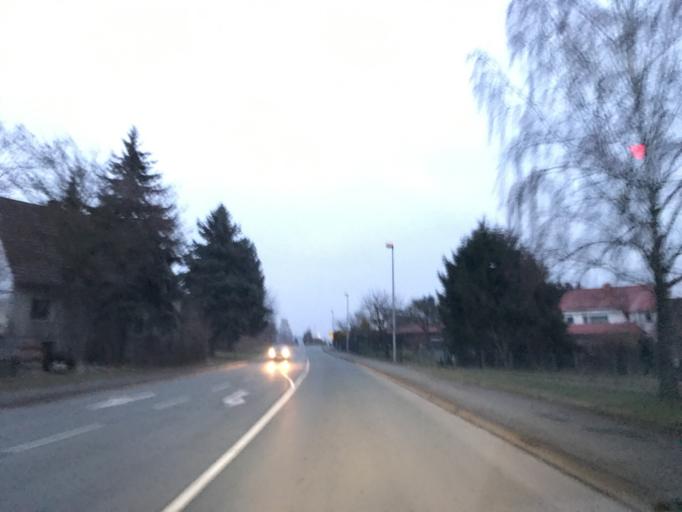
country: DE
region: Hesse
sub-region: Regierungsbezirk Kassel
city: Hofgeismar
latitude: 51.5004
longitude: 9.3816
